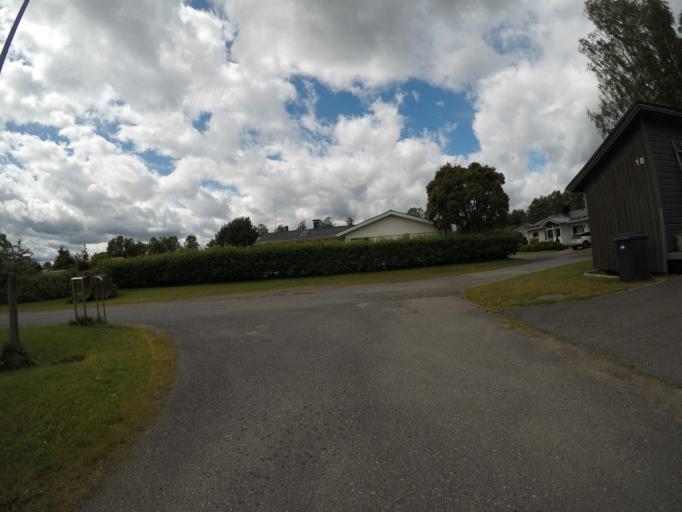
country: FI
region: Haeme
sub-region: Haemeenlinna
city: Haemeenlinna
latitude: 60.9762
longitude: 24.4304
